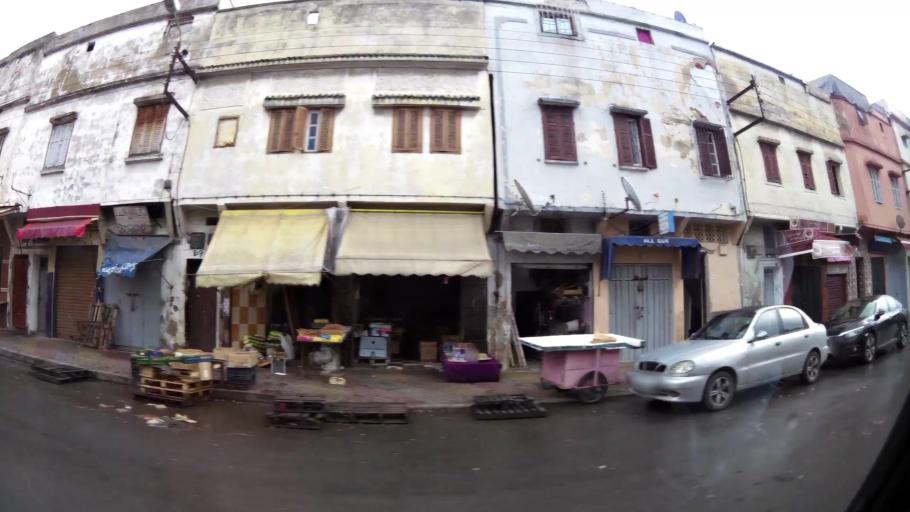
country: MA
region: Grand Casablanca
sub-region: Casablanca
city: Casablanca
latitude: 33.5672
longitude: -7.5817
